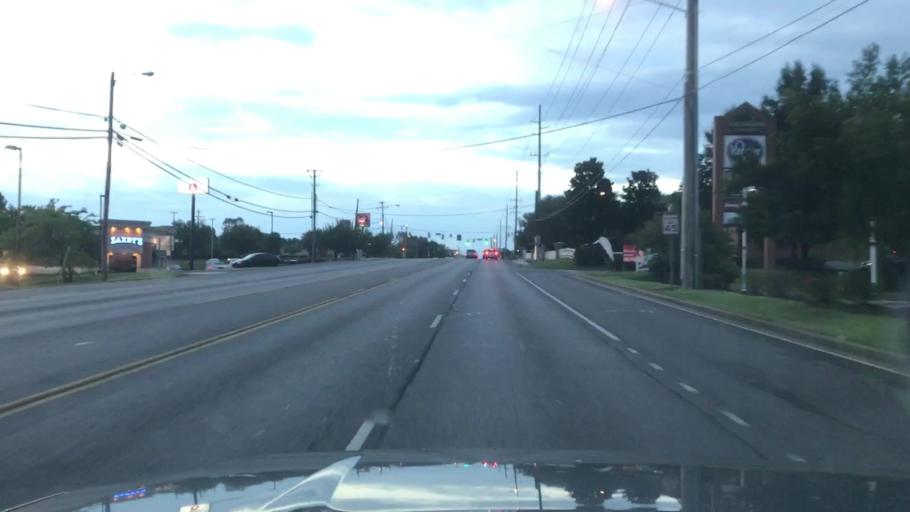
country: US
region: Tennessee
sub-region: Rutherford County
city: La Vergne
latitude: 36.0874
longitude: -86.6489
